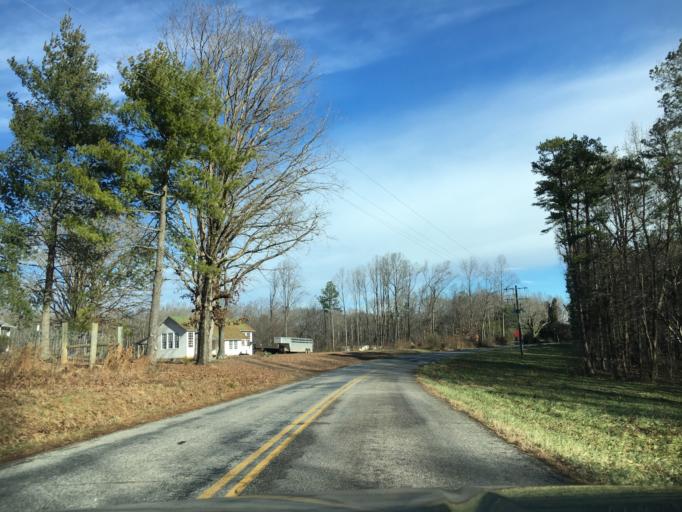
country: US
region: Virginia
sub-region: Amelia County
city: Amelia Court House
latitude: 37.3855
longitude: -78.1240
